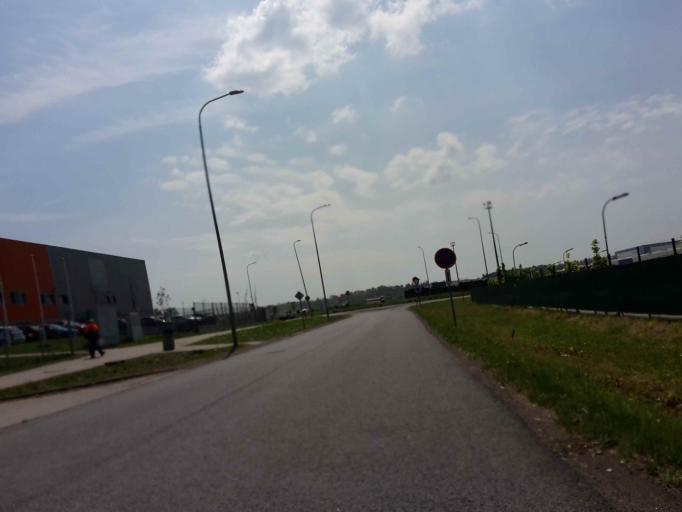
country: SK
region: Bratislavsky
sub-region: Okres Malacky
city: Malacky
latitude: 48.4191
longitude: 17.0353
